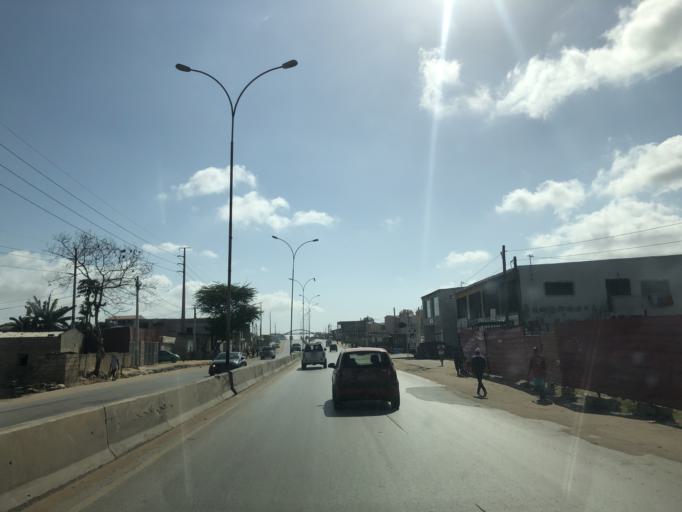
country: AO
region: Luanda
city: Luanda
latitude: -8.9065
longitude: 13.2438
